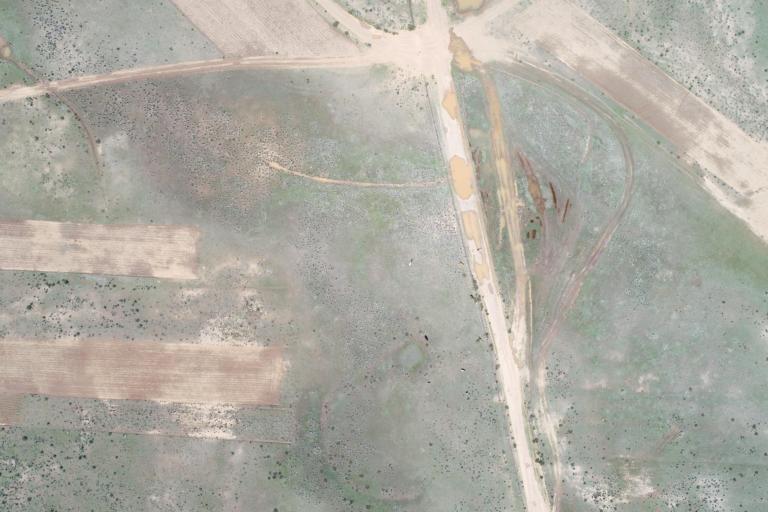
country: BO
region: La Paz
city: Patacamaya
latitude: -17.2765
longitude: -68.5091
